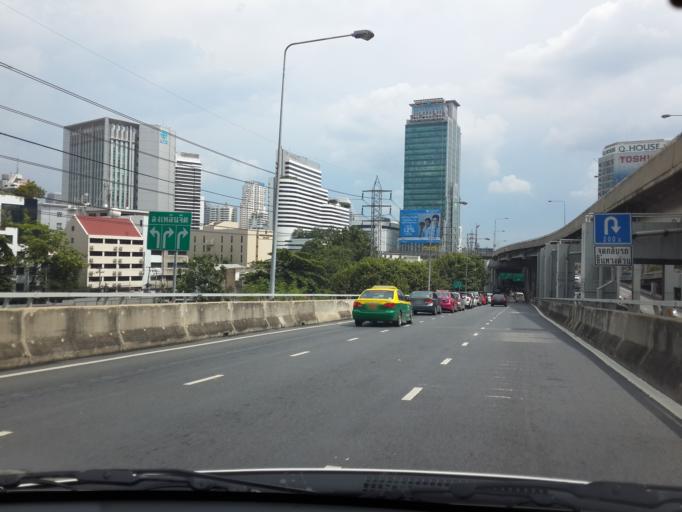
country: TH
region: Bangkok
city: Ratchathewi
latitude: 13.7456
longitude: 100.5503
